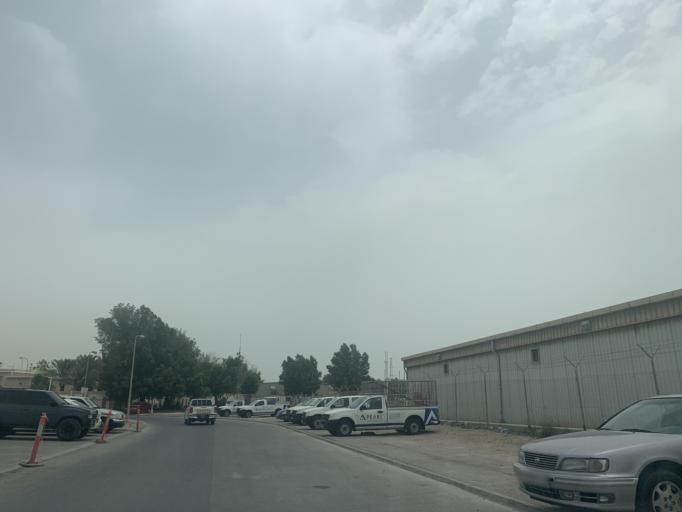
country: BH
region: Northern
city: Sitrah
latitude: 26.1787
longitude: 50.6178
